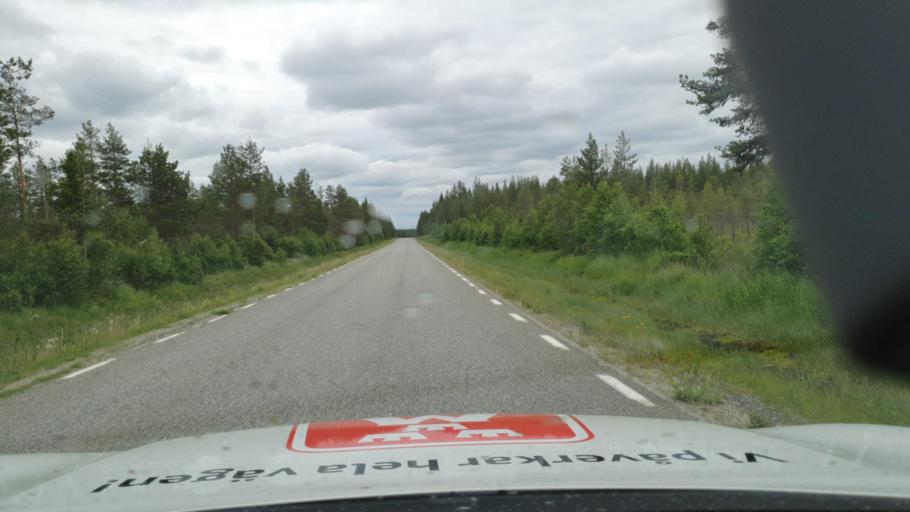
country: SE
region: Vaesterbotten
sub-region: Lycksele Kommun
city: Soderfors
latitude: 64.2654
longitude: 18.2041
